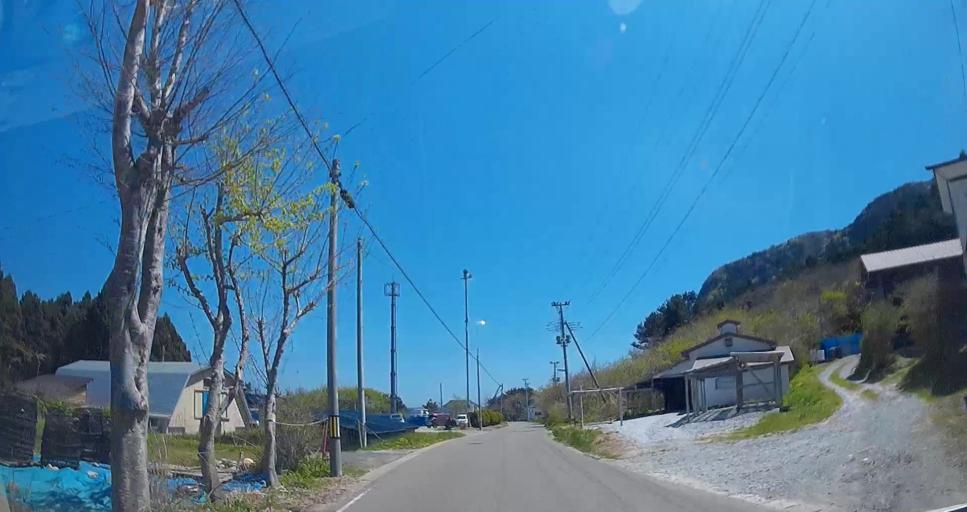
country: JP
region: Aomori
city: Mutsu
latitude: 41.3981
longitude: 141.4493
